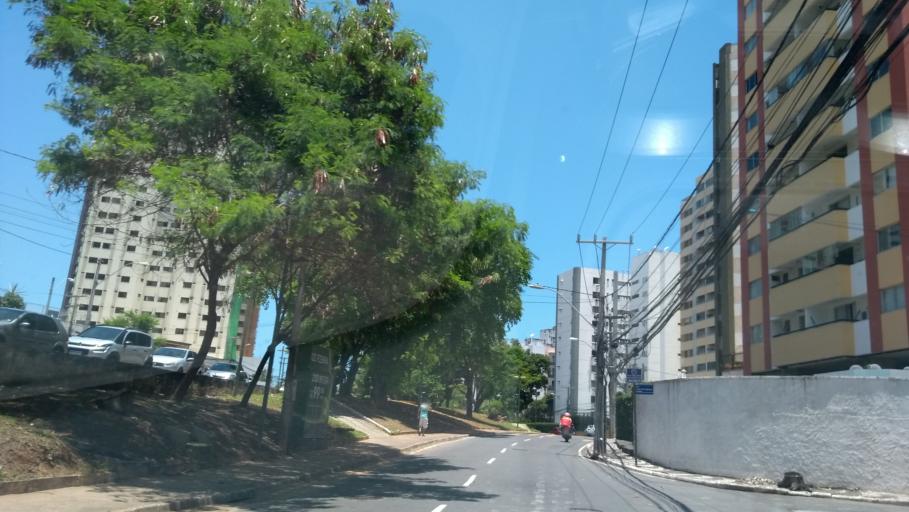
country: BR
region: Bahia
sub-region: Salvador
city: Salvador
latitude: -12.9906
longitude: -38.4527
